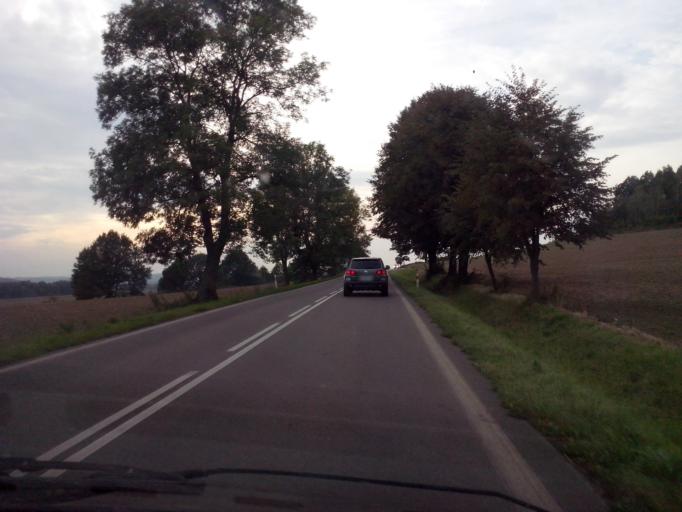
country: PL
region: Subcarpathian Voivodeship
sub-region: Powiat przeworski
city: Jawornik Polski
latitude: 49.8297
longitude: 22.3022
